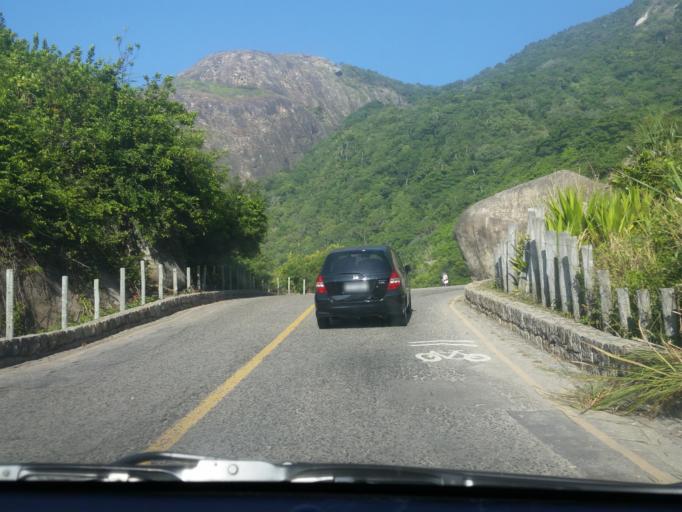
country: BR
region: Rio de Janeiro
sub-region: Nilopolis
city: Nilopolis
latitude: -23.0409
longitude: -43.5061
